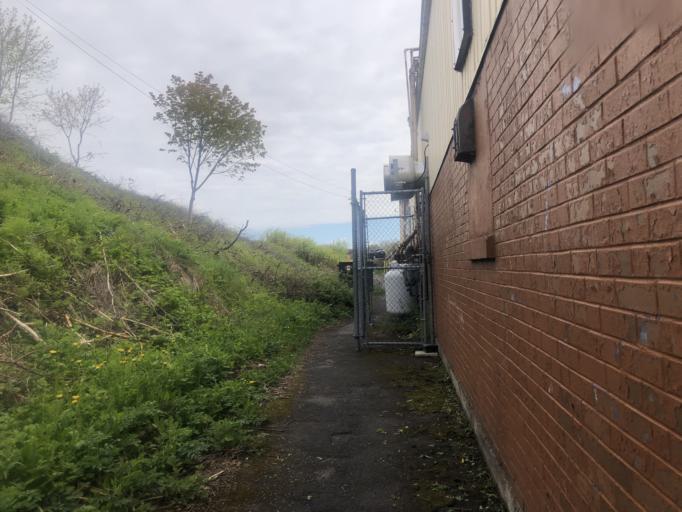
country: CA
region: New Brunswick
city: Saint John
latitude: 45.2773
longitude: -66.0795
